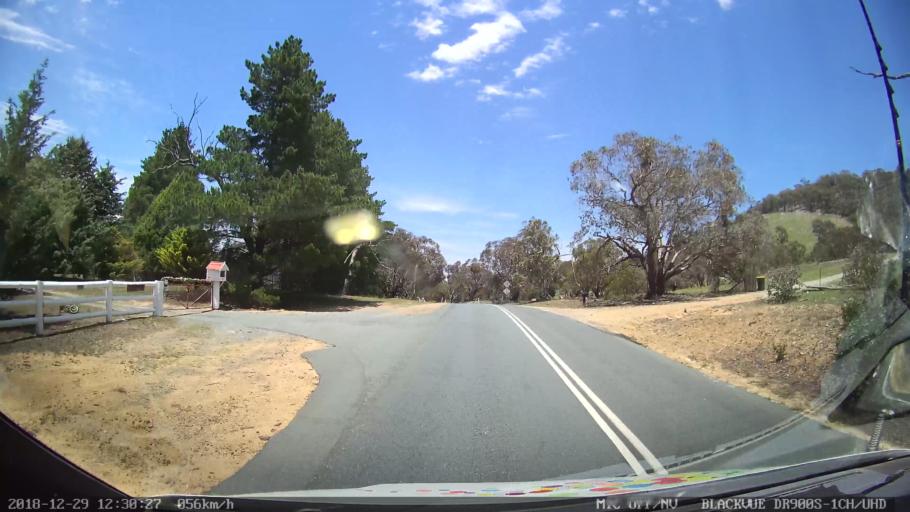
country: AU
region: Australian Capital Territory
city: Macarthur
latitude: -35.5061
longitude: 149.2330
